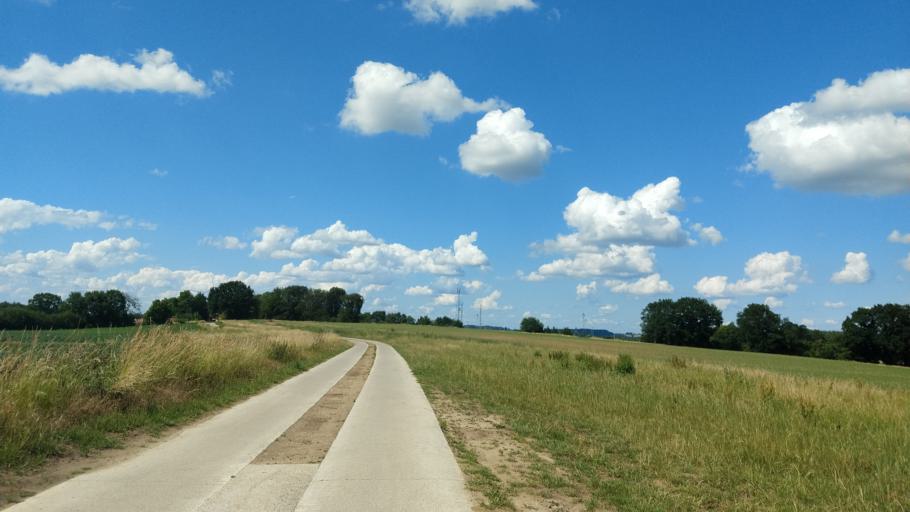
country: BE
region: Flanders
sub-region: Provincie Vlaams-Brabant
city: Bierbeek
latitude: 50.8230
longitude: 4.7521
